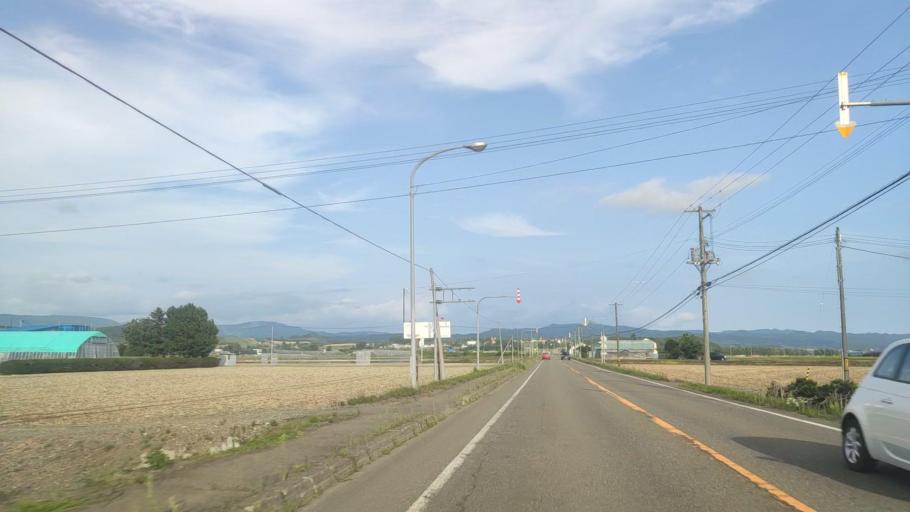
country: JP
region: Hokkaido
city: Iwamizawa
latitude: 43.0280
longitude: 141.8175
